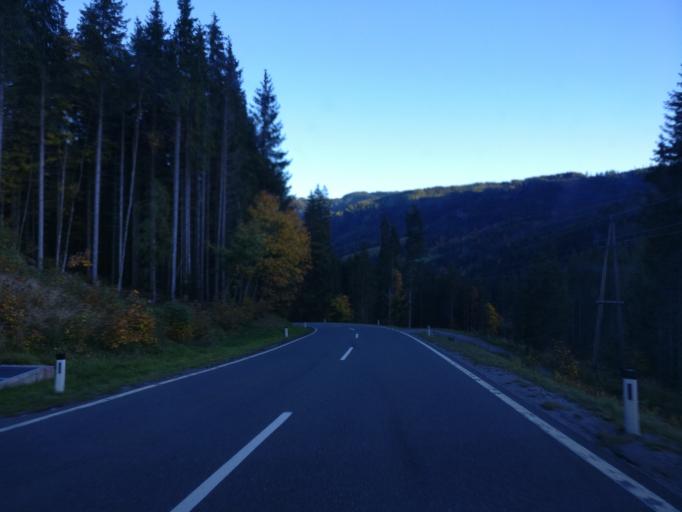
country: AT
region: Salzburg
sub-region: Politischer Bezirk Sankt Johann im Pongau
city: Muhlbach am Hochkonig
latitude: 47.3886
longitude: 13.1003
